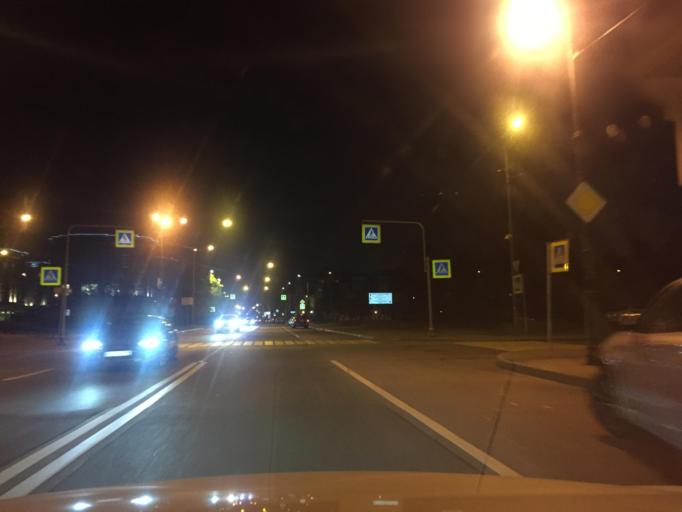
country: RU
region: Leningrad
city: Krestovskiy ostrov
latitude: 59.9740
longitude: 30.2637
